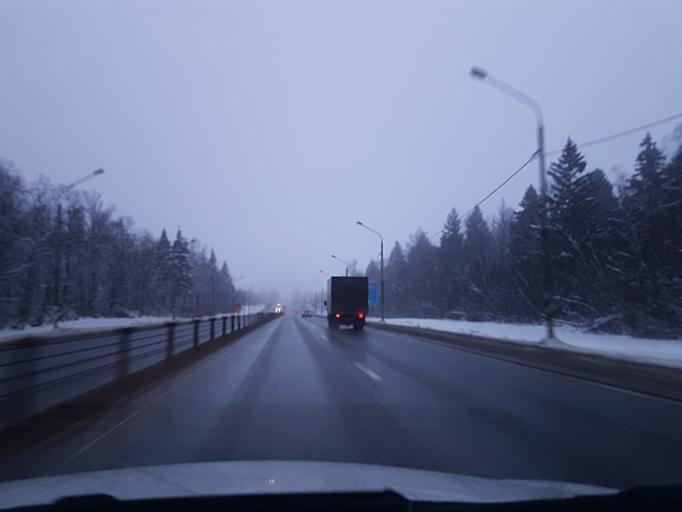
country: RU
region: Moskovskaya
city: Klin
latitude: 56.2756
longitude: 36.8353
